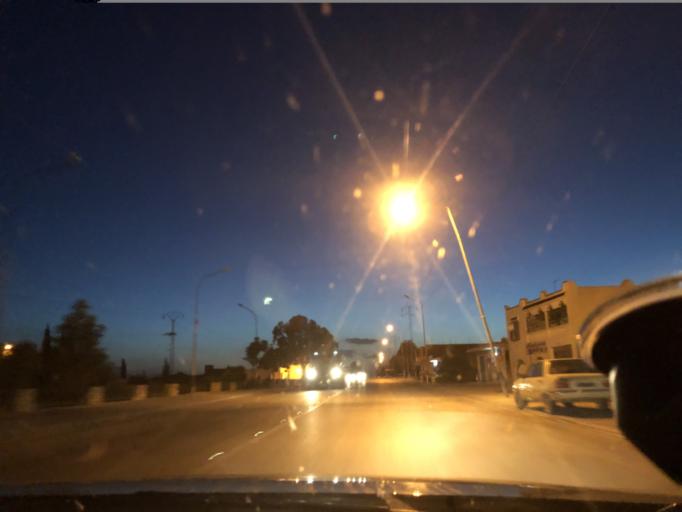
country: TN
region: Al Qasrayn
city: Kasserine
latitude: 35.2549
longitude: 9.0205
